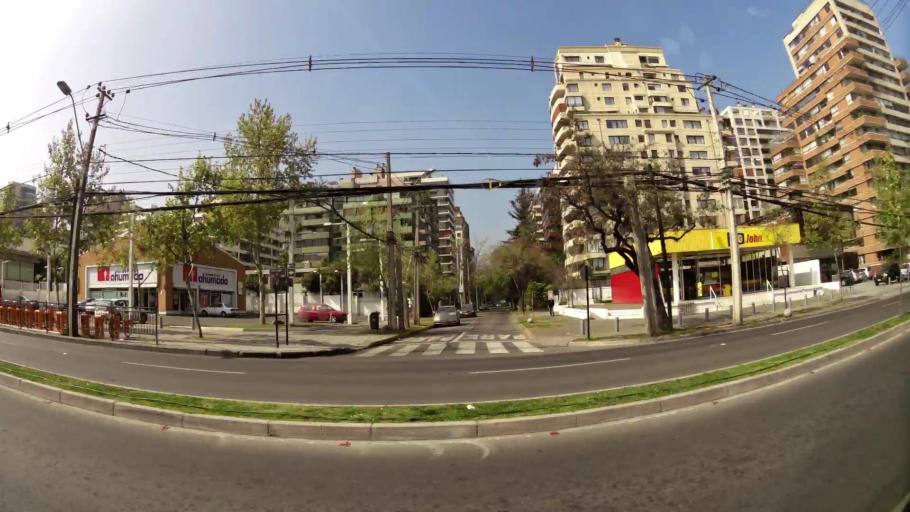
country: CL
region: Santiago Metropolitan
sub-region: Provincia de Santiago
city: Villa Presidente Frei, Nunoa, Santiago, Chile
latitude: -33.4051
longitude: -70.5974
